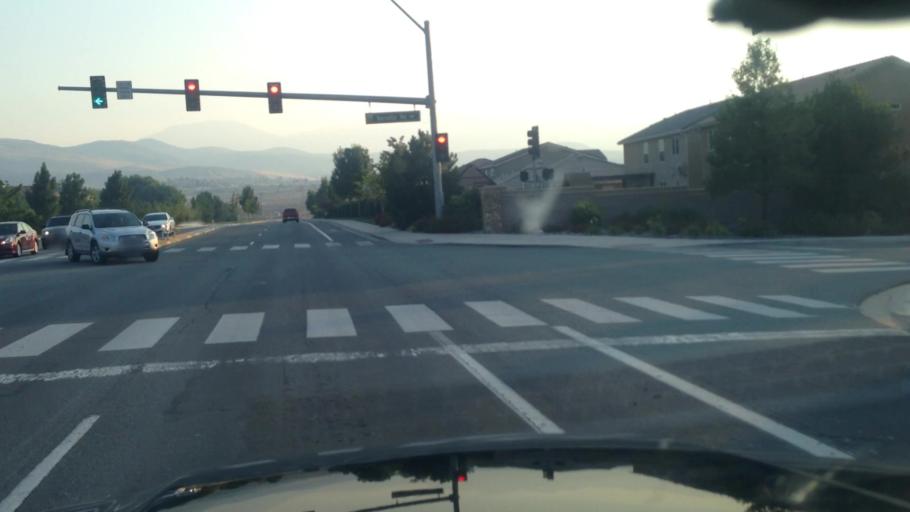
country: US
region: Nevada
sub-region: Storey County
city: Virginia City
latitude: 39.4048
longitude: -119.7361
